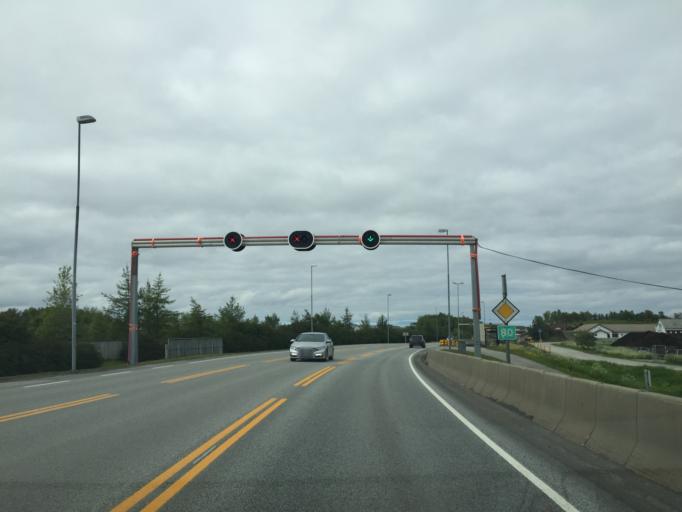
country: NO
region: Nordland
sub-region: Bodo
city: Bodo
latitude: 67.2759
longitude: 14.4421
